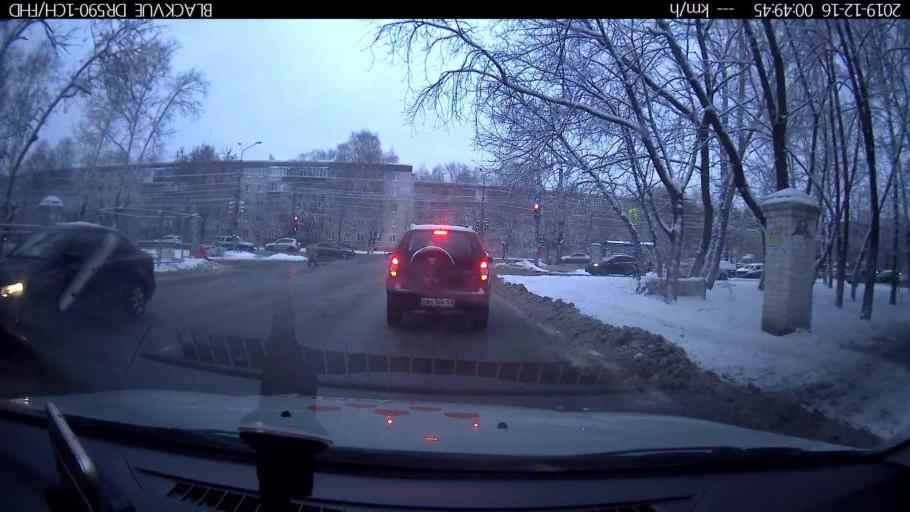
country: RU
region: Nizjnij Novgorod
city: Gorbatovka
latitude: 56.3127
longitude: 43.8581
